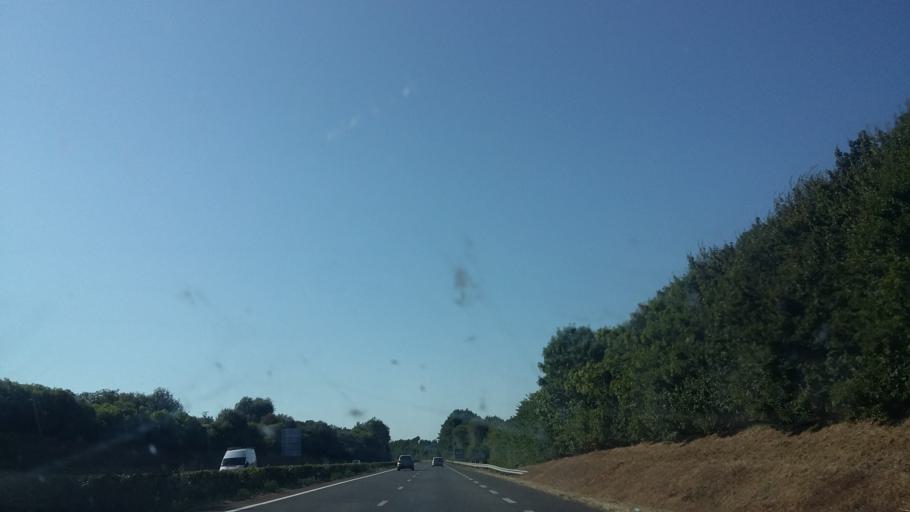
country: FR
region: Pays de la Loire
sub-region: Departement de la Vendee
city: Challans
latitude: 46.8573
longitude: -1.8547
